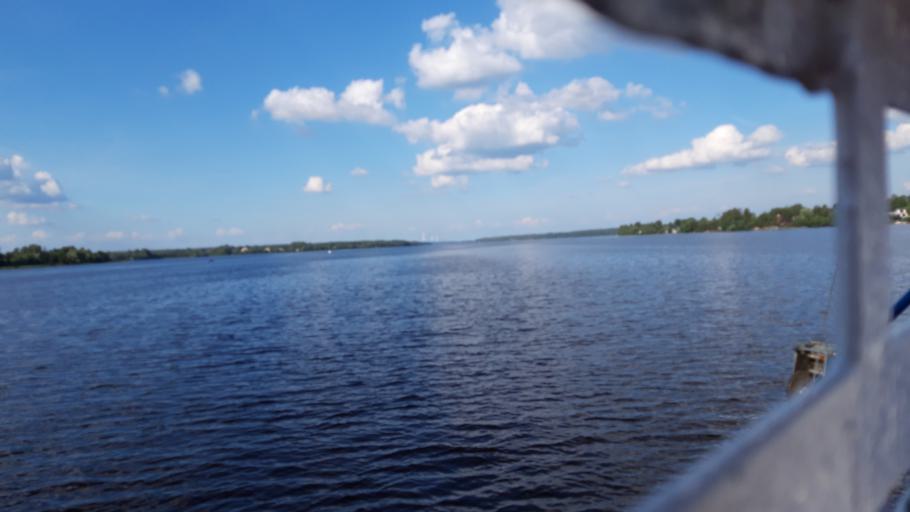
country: RU
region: Tverskaya
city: Konakovo
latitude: 56.6576
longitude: 36.6402
